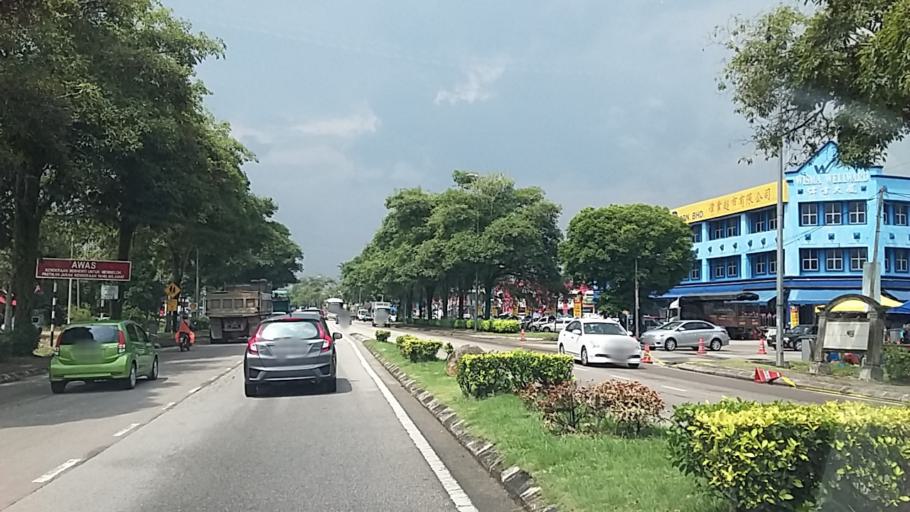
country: MY
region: Johor
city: Parit Raja
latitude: 1.8658
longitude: 103.1135
